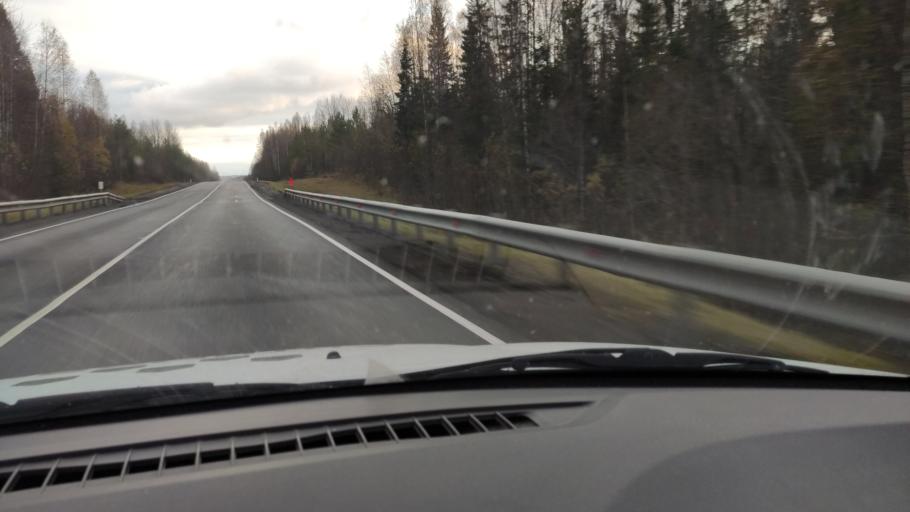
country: RU
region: Kirov
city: Omutninsk
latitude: 58.7435
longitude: 52.0651
